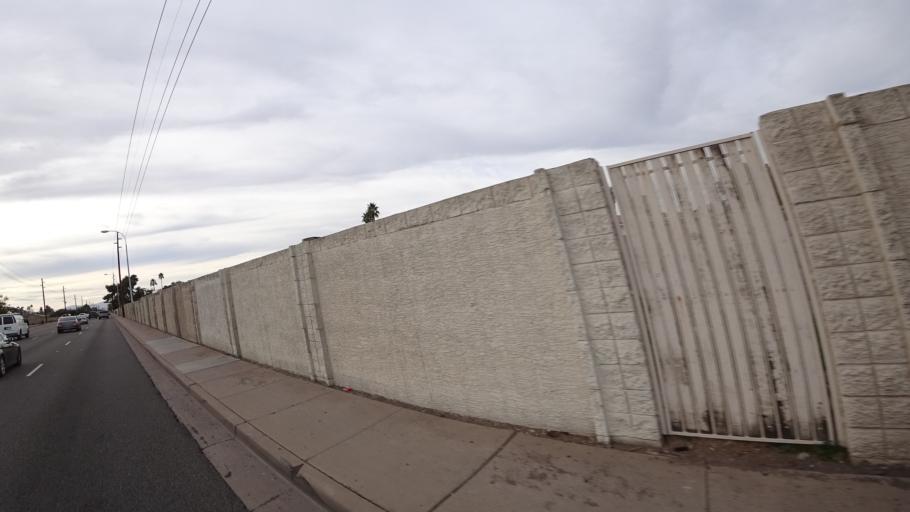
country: US
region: Arizona
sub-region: Maricopa County
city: Glendale
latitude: 33.5676
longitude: -112.1540
